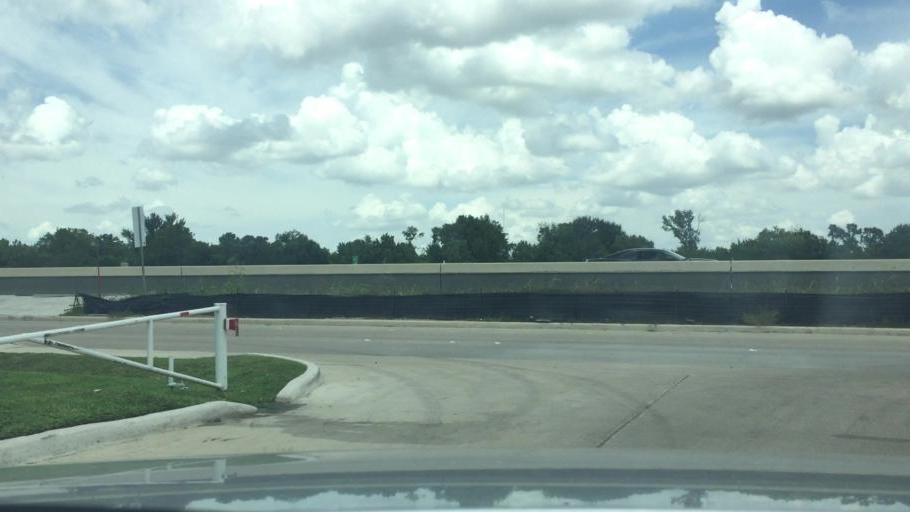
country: US
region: Texas
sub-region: Harris County
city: Jersey Village
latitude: 29.8628
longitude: -95.5272
